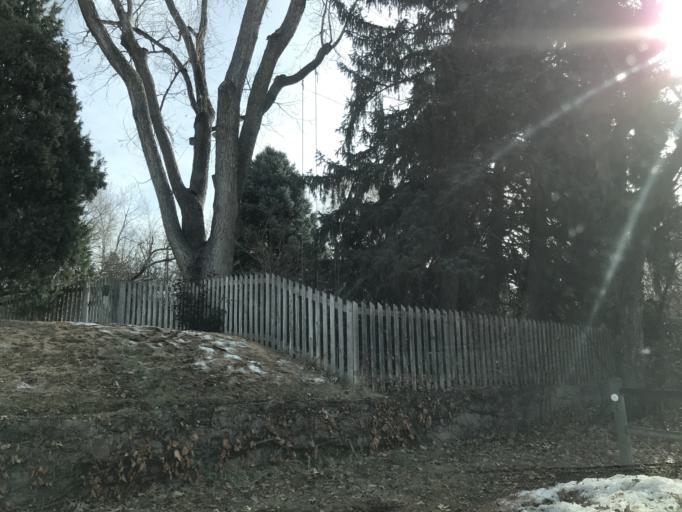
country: US
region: Colorado
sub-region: Arapahoe County
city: Littleton
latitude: 39.6099
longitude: -105.0103
